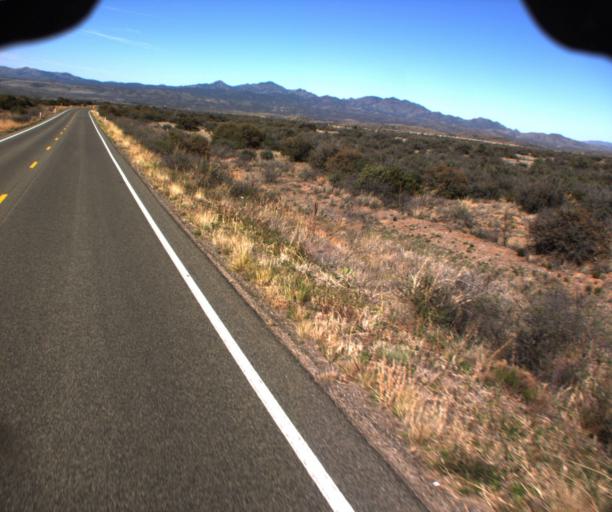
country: US
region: Arizona
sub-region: Yavapai County
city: Prescott
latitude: 34.3972
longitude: -112.6291
